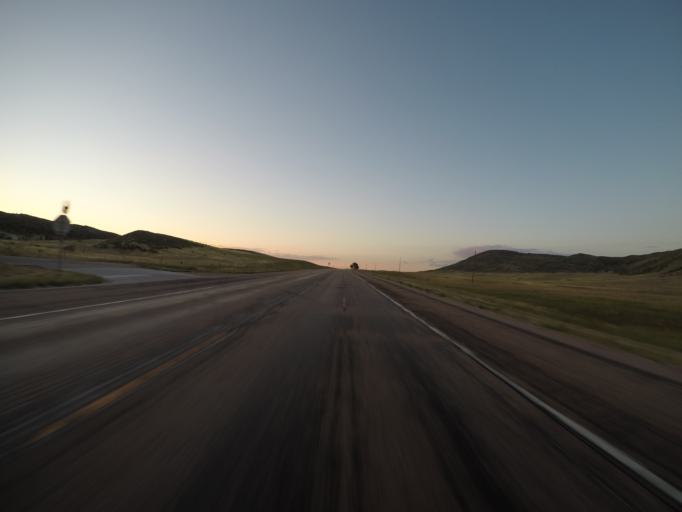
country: US
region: Colorado
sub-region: Larimer County
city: Laporte
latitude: 40.7412
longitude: -105.1707
